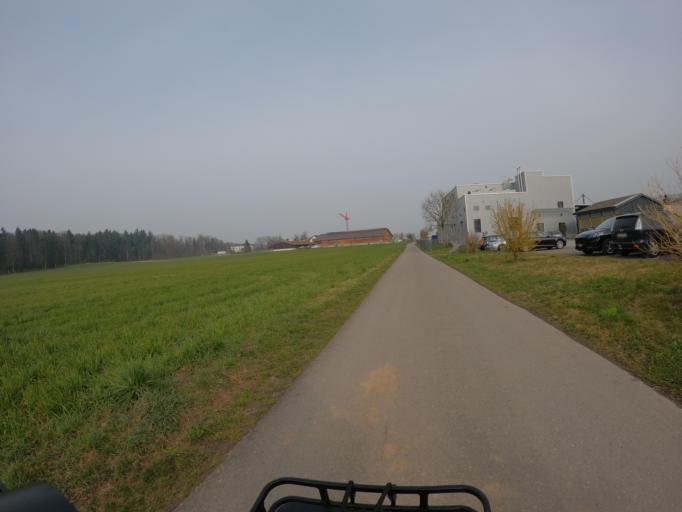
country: CH
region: Aargau
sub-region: Bezirk Bremgarten
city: Bremgarten
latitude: 47.3408
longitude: 8.3532
